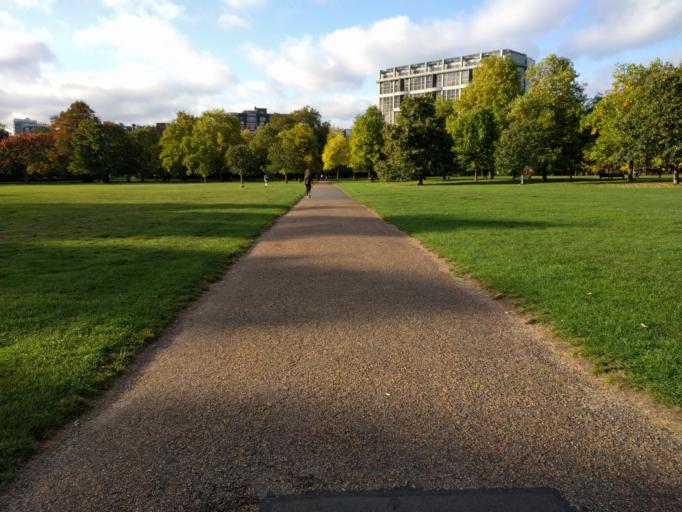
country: GB
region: England
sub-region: Greater London
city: Kensington
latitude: 51.5042
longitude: -0.1862
